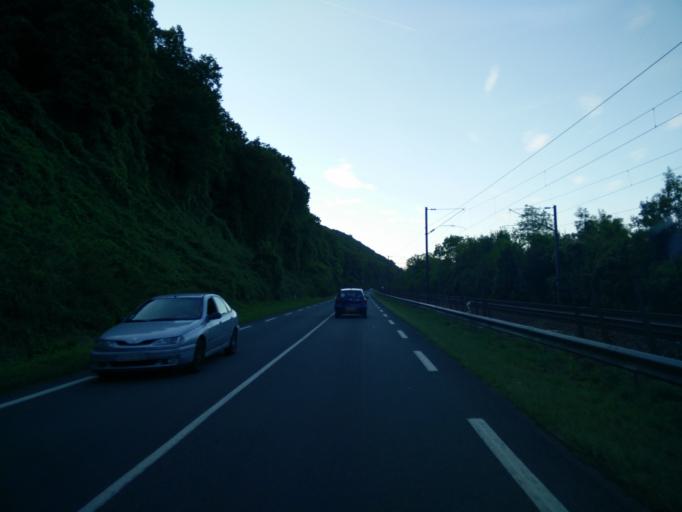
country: FR
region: Ile-de-France
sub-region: Departement des Yvelines
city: Bennecourt
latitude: 49.0457
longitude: 1.5315
